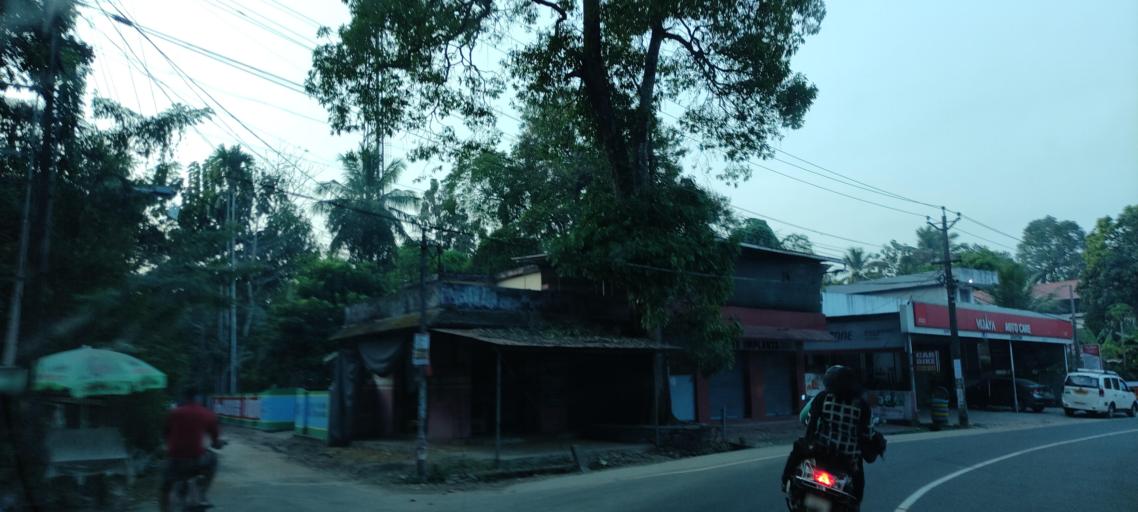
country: IN
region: Kerala
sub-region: Alappuzha
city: Mavelikara
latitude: 9.2689
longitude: 76.5381
